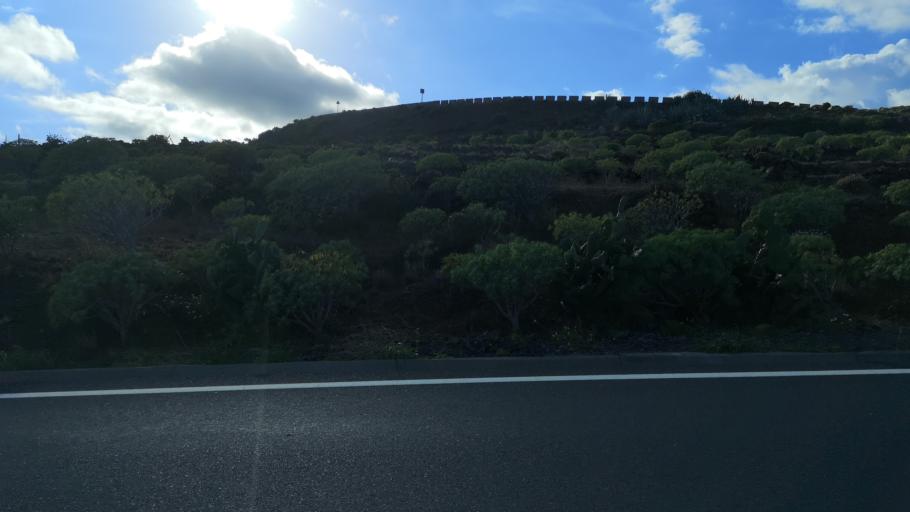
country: ES
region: Canary Islands
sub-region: Provincia de Santa Cruz de Tenerife
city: San Sebastian de la Gomera
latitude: 28.0857
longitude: -17.1420
